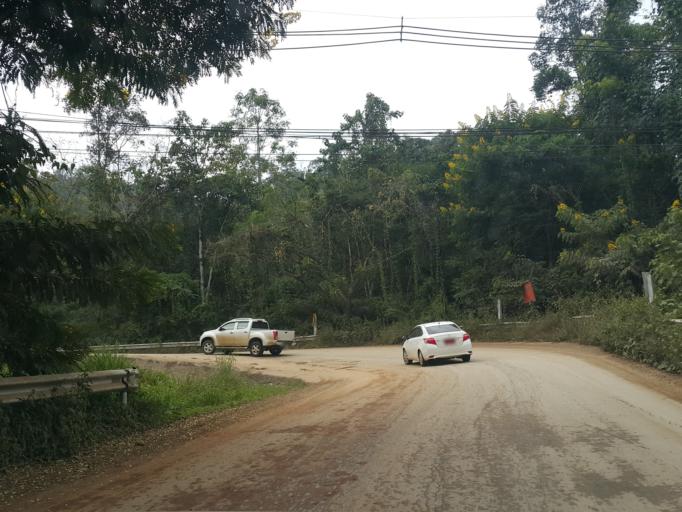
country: TH
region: Chiang Mai
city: Mae Taeng
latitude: 19.1545
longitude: 98.6930
